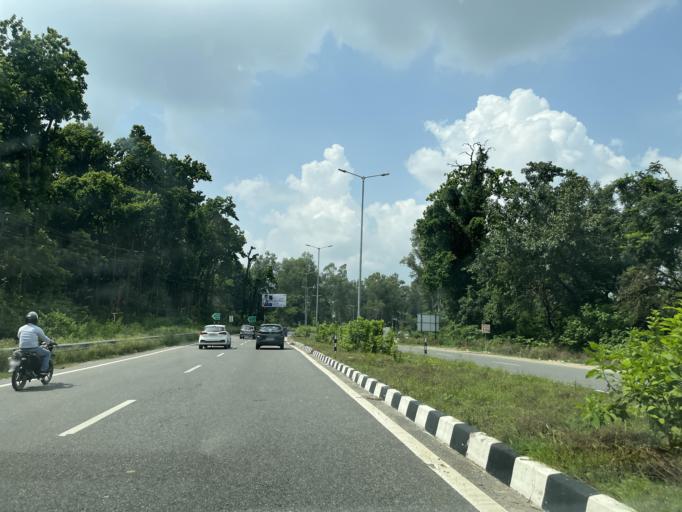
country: IN
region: Uttarakhand
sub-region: Dehradun
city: Raipur
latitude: 30.2496
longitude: 78.0943
